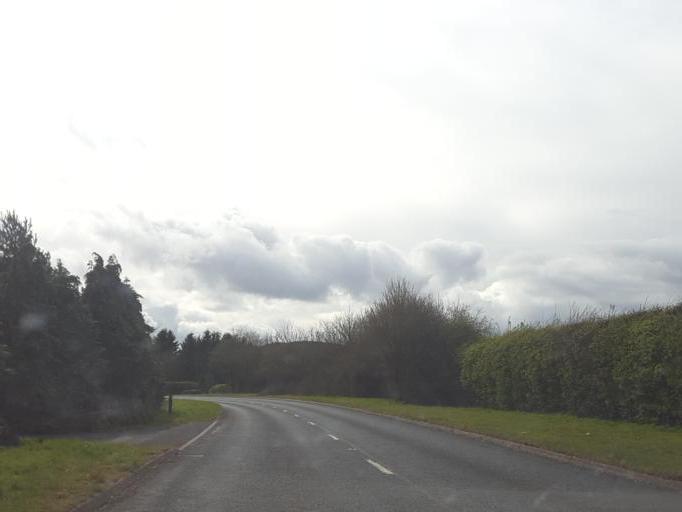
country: GB
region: England
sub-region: Worcestershire
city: Leigh
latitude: 52.1453
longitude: -2.3279
